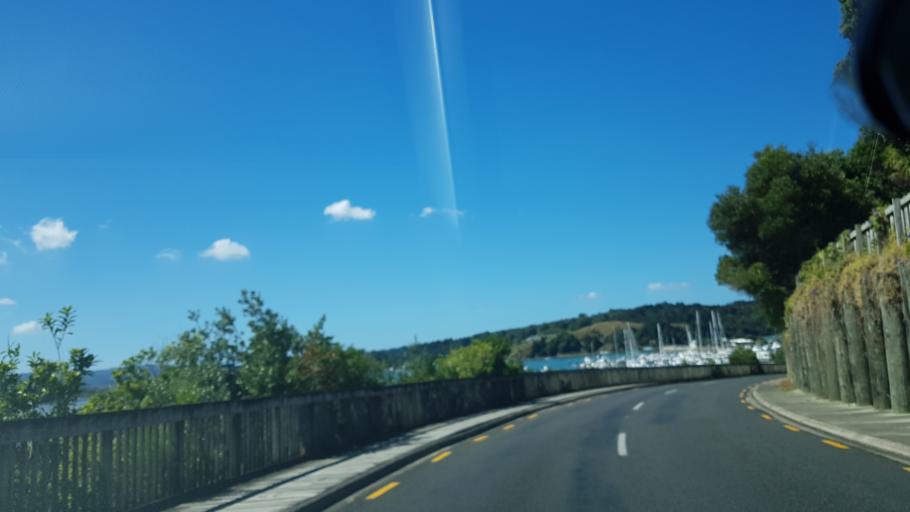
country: NZ
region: Auckland
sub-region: Auckland
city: Warkworth
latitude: -36.3925
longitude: 174.7226
